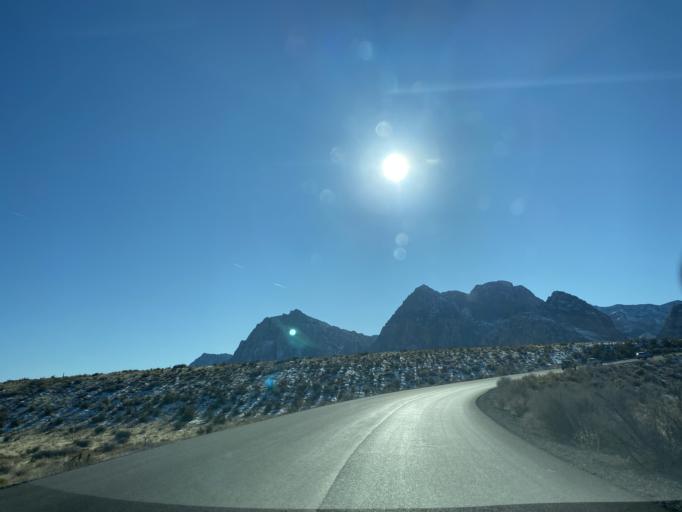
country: US
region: Nevada
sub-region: Clark County
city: Summerlin South
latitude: 36.1389
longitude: -115.4671
